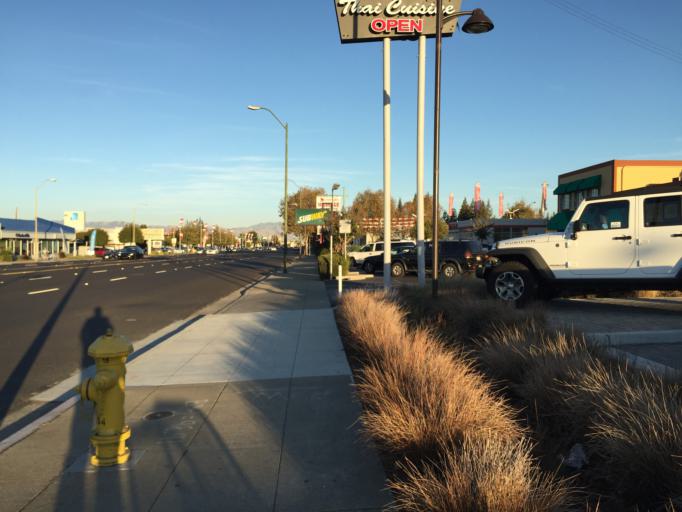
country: US
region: California
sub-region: Santa Clara County
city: Cupertino
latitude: 37.3229
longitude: -121.9907
